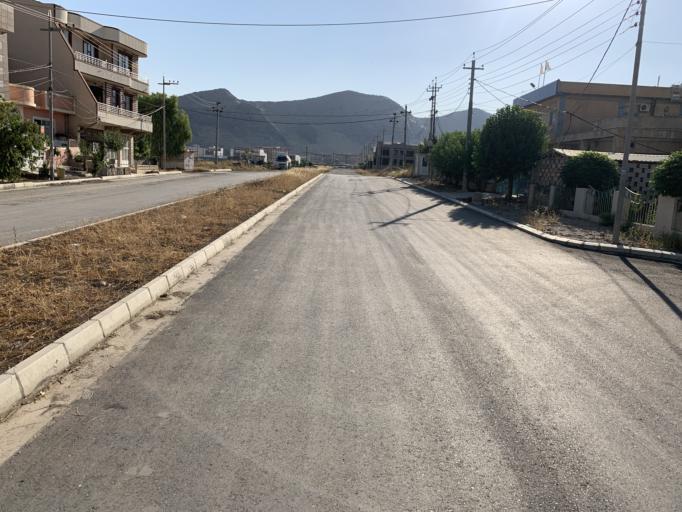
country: IQ
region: As Sulaymaniyah
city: Raniye
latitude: 36.2391
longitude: 44.8710
